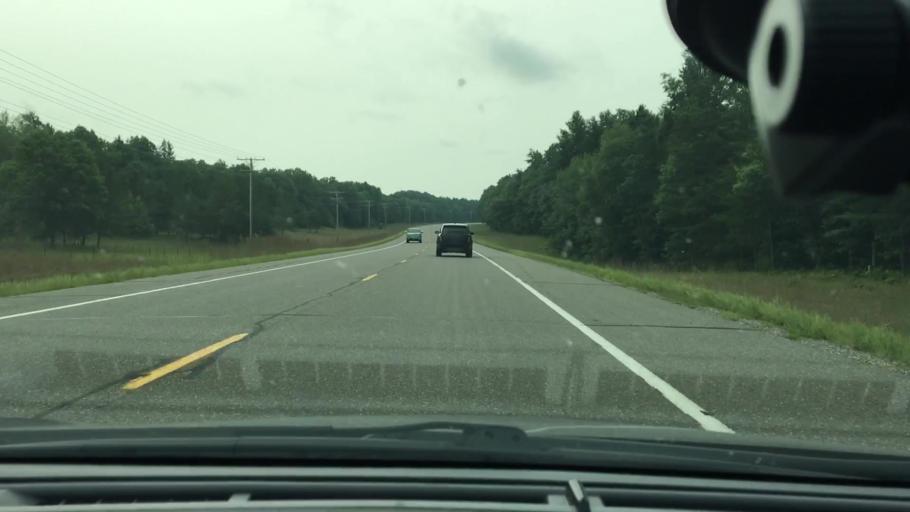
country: US
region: Minnesota
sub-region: Crow Wing County
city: Cross Lake
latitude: 46.6075
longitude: -94.1315
